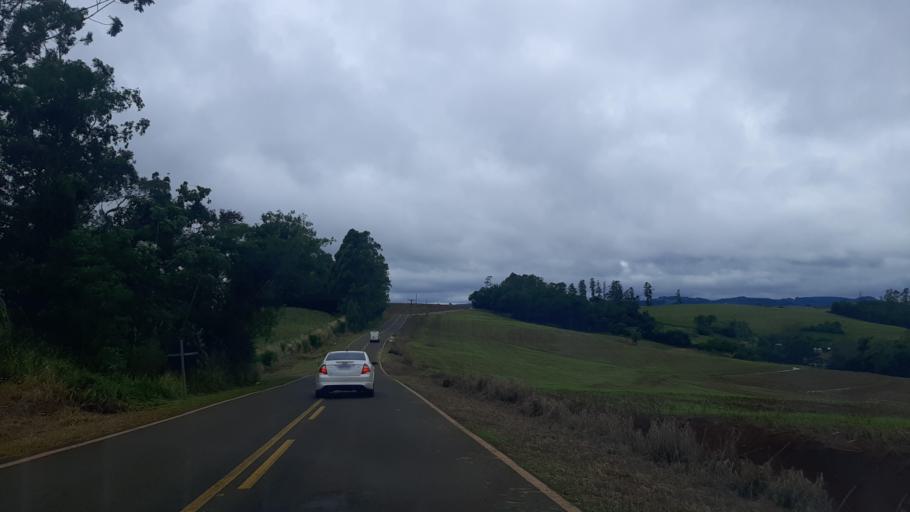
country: BR
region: Parana
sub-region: Ampere
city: Ampere
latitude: -25.9544
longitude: -53.4556
